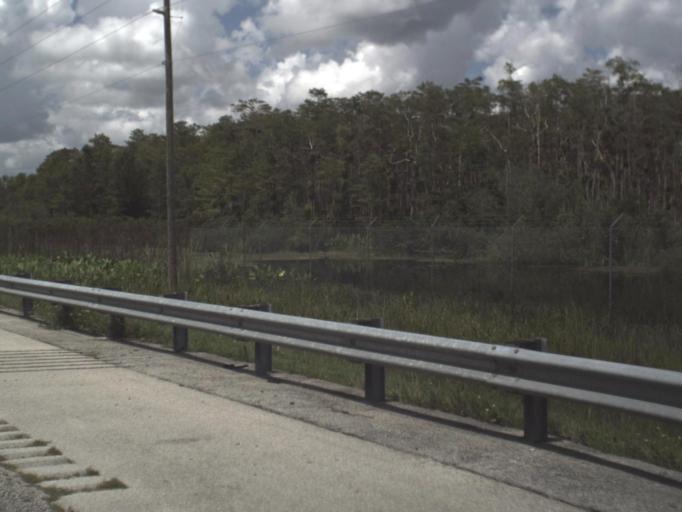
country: US
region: Florida
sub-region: Collier County
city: Immokalee
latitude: 26.1701
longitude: -81.0070
